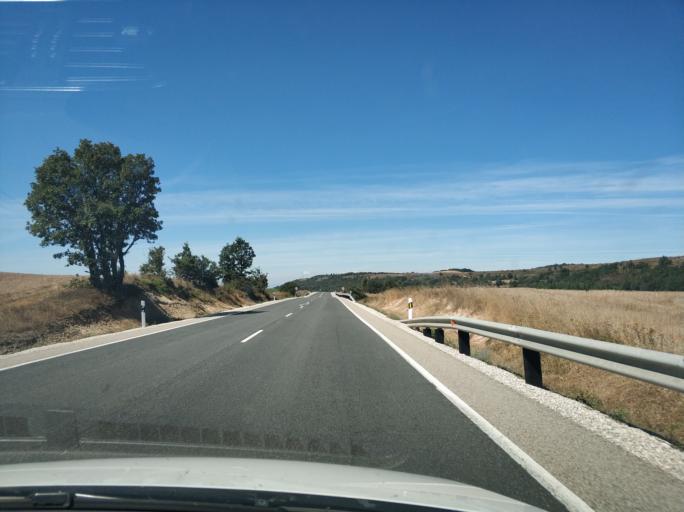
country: ES
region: Castille and Leon
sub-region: Provincia de Burgos
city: Basconcillos del Tozo
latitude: 42.6758
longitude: -3.9396
